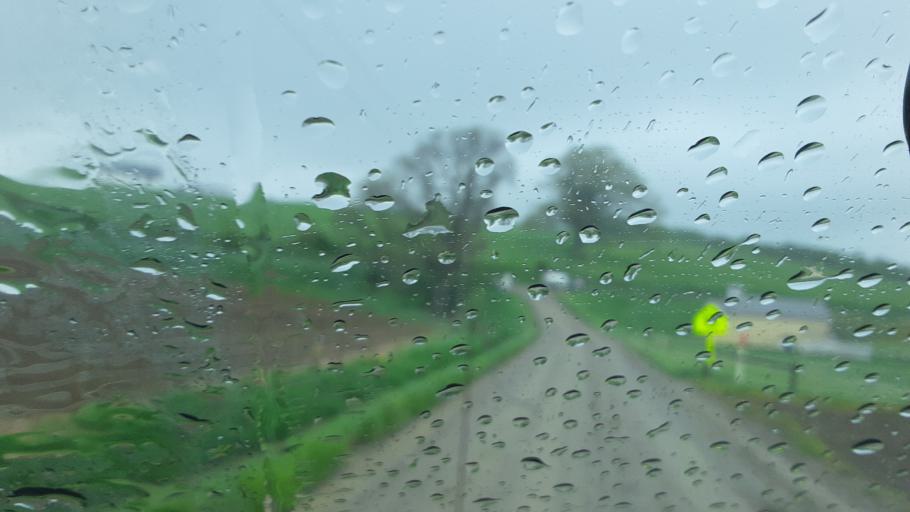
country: US
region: Ohio
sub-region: Holmes County
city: Millersburg
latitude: 40.4770
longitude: -81.8326
